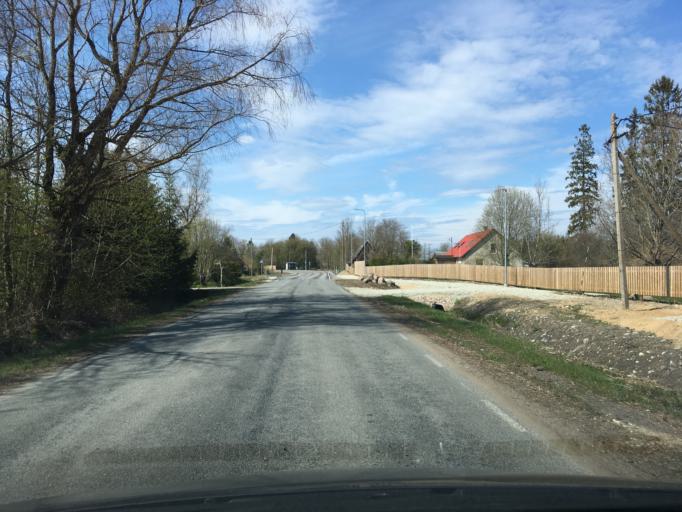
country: EE
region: Harju
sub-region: Raasiku vald
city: Arukula
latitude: 59.4126
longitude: 25.1243
